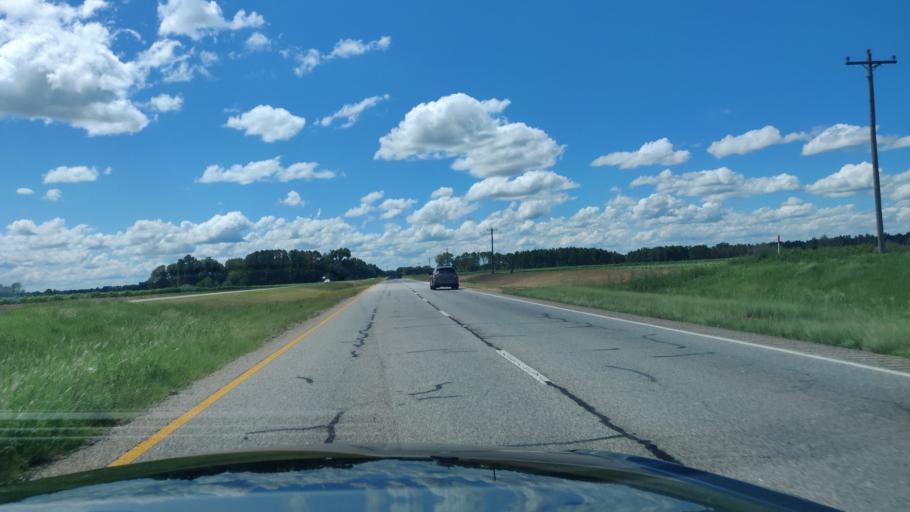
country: US
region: Georgia
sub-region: Stewart County
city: Richland
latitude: 31.9892
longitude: -84.6318
